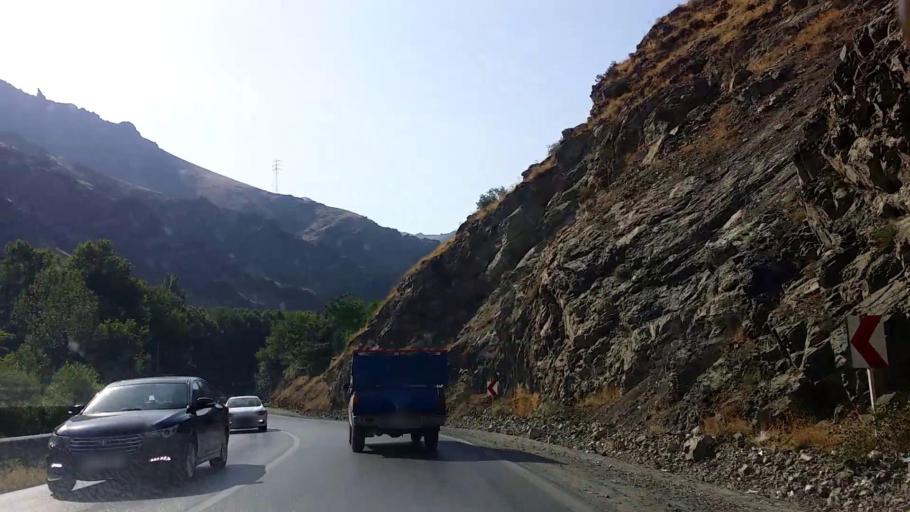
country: IR
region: Alborz
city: Karaj
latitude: 35.8713
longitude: 51.0484
